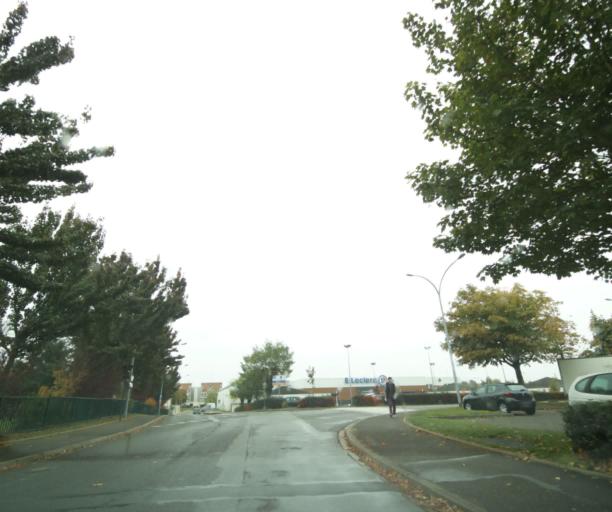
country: FR
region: Centre
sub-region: Departement d'Eure-et-Loir
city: Dreux
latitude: 48.7378
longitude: 1.3470
